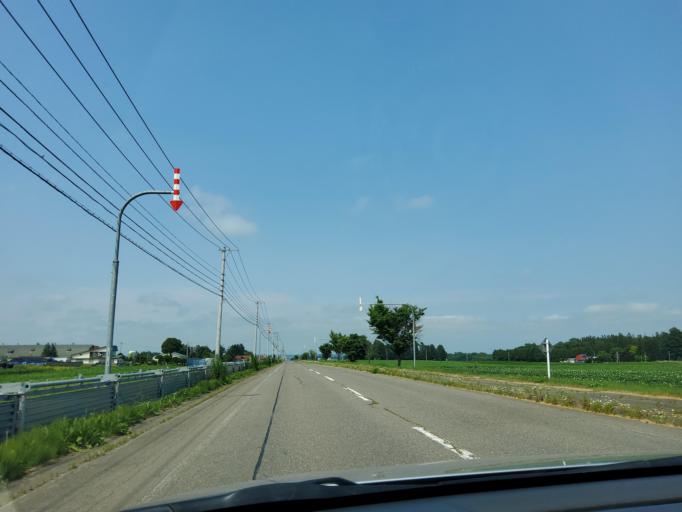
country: JP
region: Hokkaido
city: Obihiro
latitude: 42.8733
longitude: 143.0260
